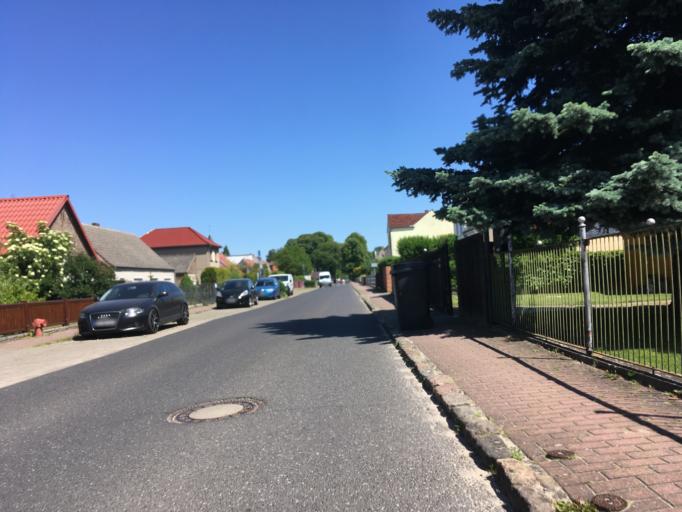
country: DE
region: Berlin
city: Muggelheim
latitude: 52.3934
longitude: 13.7079
